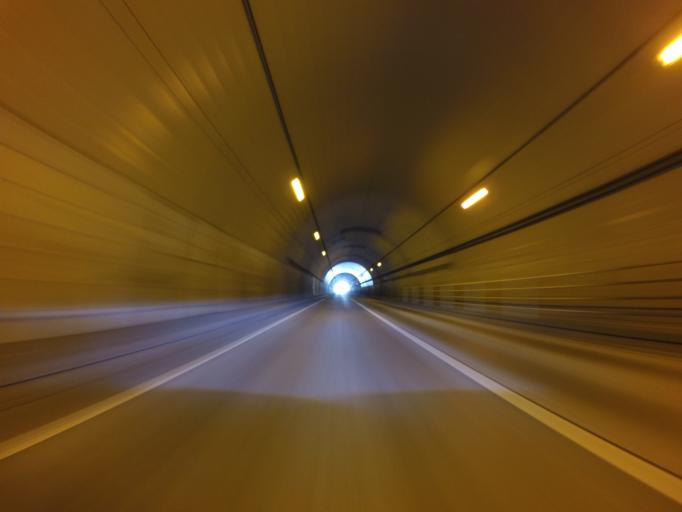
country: JP
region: Shizuoka
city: Shizuoka-shi
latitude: 35.0878
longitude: 138.3760
